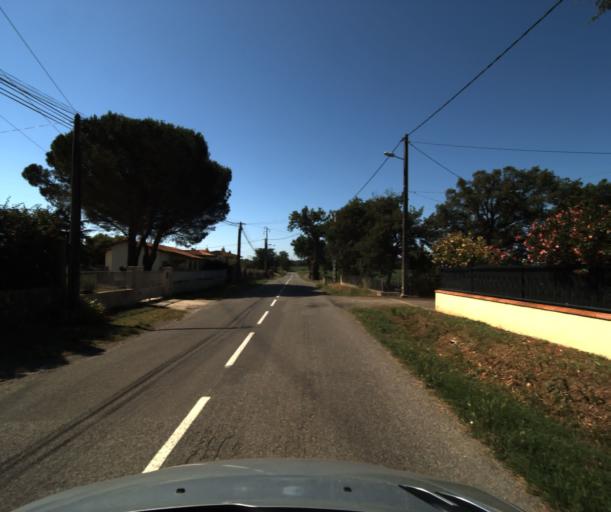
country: FR
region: Midi-Pyrenees
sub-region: Departement de la Haute-Garonne
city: Saubens
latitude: 43.4879
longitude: 1.3518
